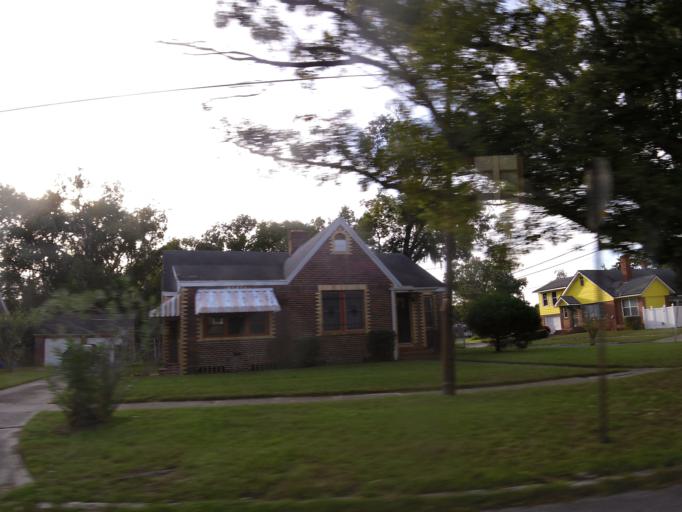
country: US
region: Florida
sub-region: Duval County
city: Jacksonville
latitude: 30.3785
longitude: -81.6568
